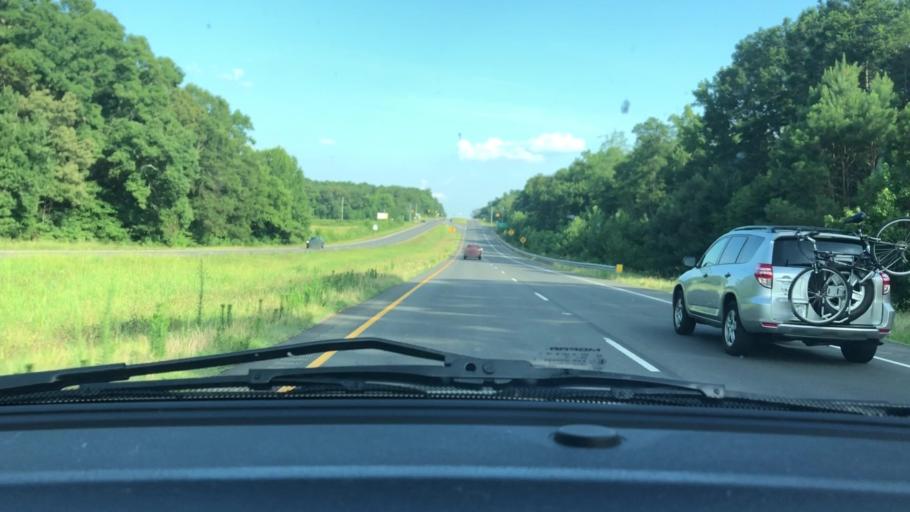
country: US
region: North Carolina
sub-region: Chatham County
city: Siler City
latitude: 35.6346
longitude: -79.3719
